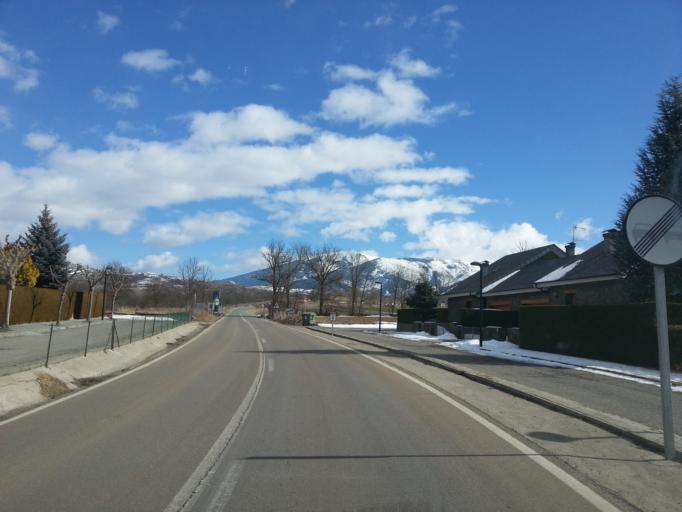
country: ES
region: Catalonia
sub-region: Provincia de Girona
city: Llivia
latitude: 42.4616
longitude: 1.9892
